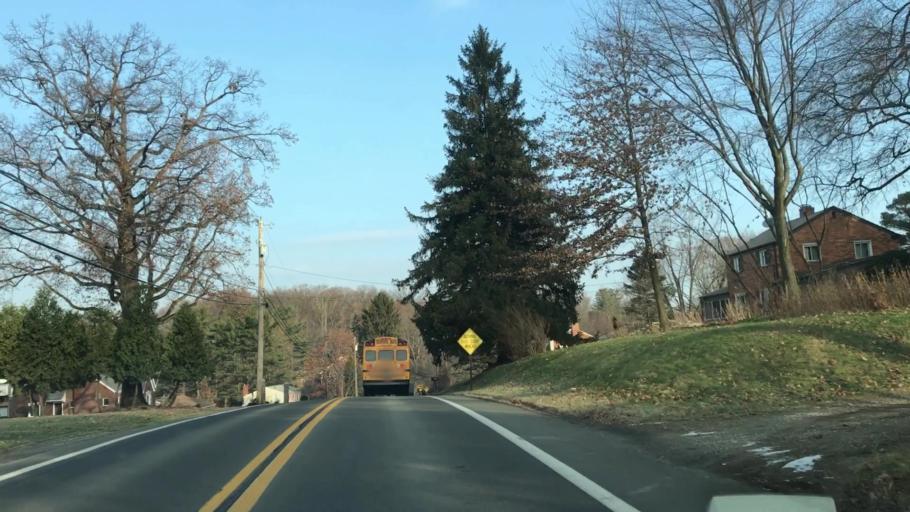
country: US
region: Pennsylvania
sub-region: Allegheny County
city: Franklin Park
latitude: 40.5731
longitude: -80.0781
